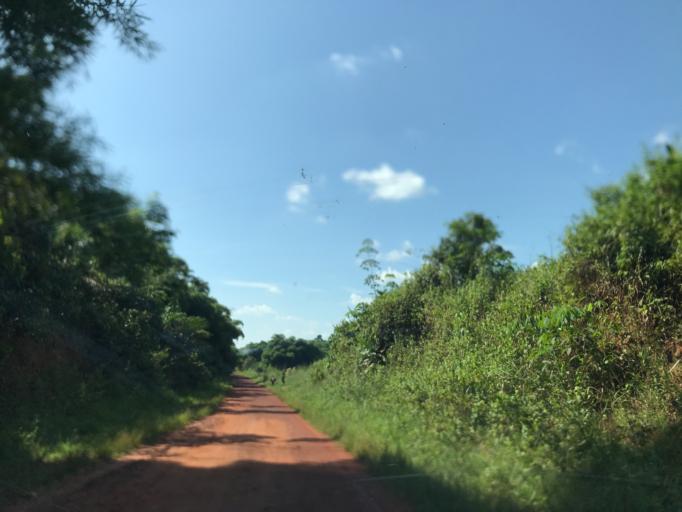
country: CD
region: Eastern Province
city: Kisangani
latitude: 1.2757
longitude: 25.2782
